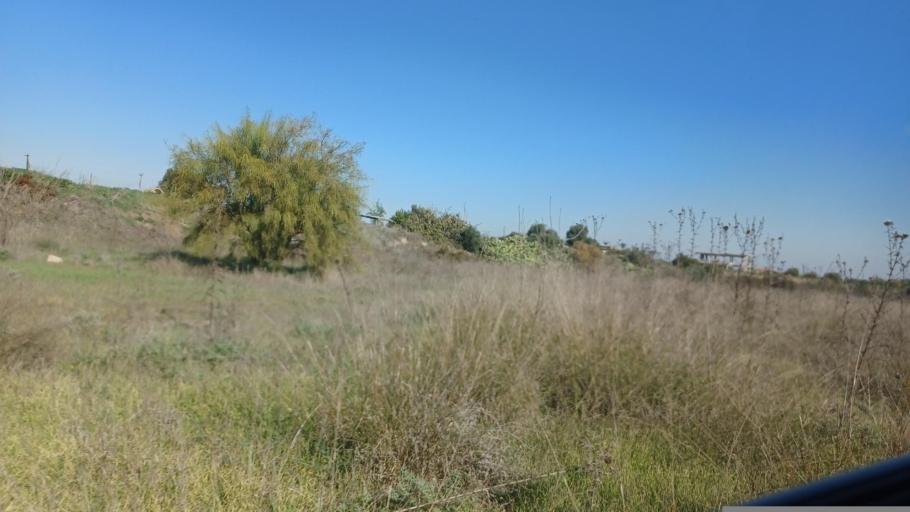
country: CY
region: Lefkosia
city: Dali
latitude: 35.0218
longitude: 33.4004
